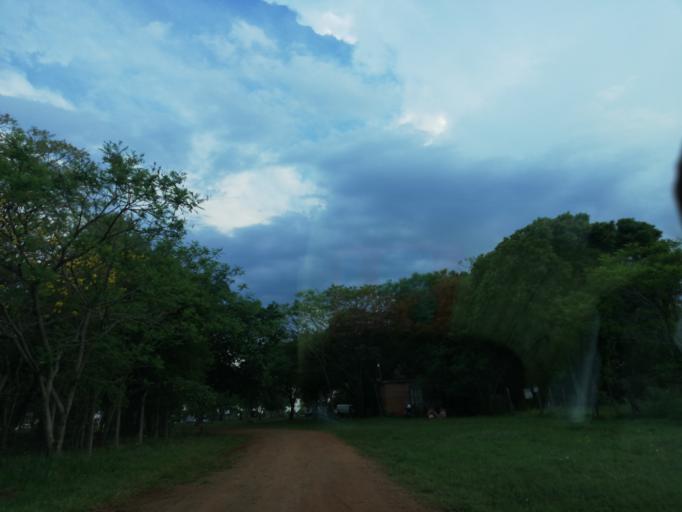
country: AR
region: Misiones
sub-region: Departamento de Capital
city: Posadas
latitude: -27.4022
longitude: -55.9731
